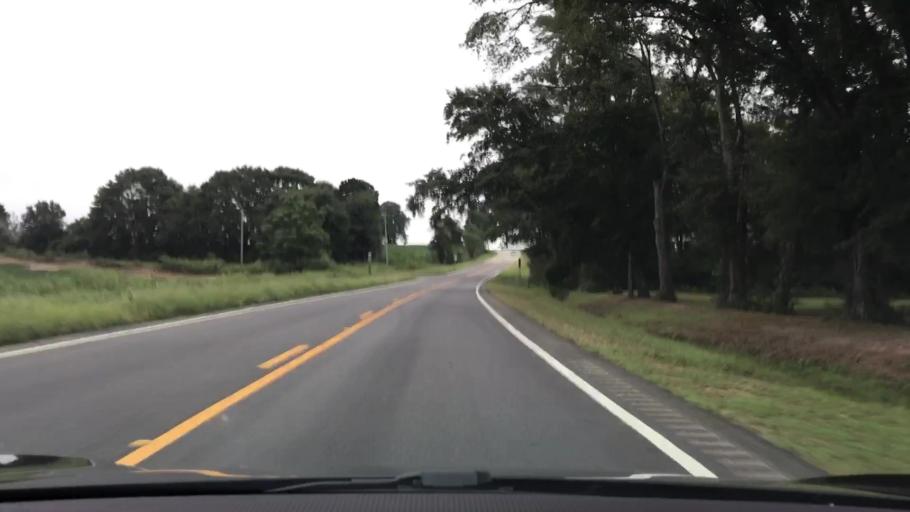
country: US
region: Alabama
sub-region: Covington County
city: Opp
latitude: 31.2848
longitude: -86.1525
